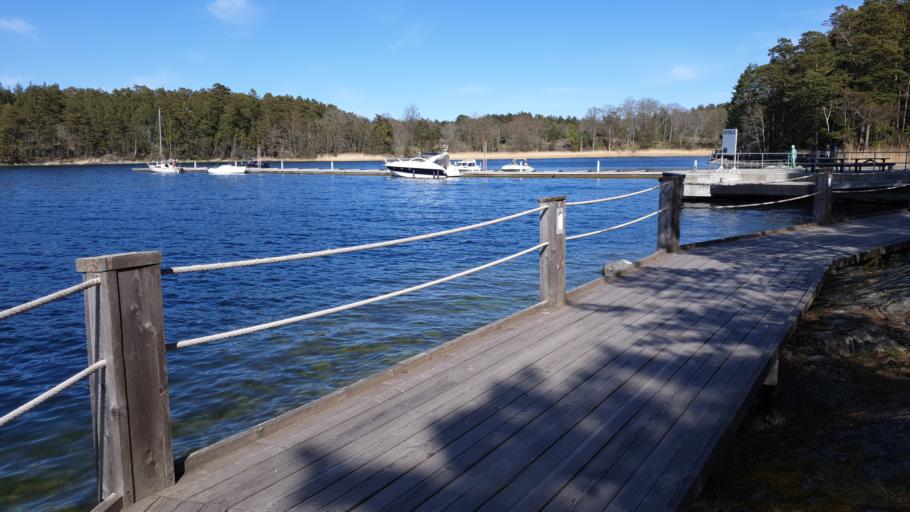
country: SE
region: Stockholm
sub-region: Varmdo Kommun
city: Gustavsberg
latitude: 59.3075
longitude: 18.3454
